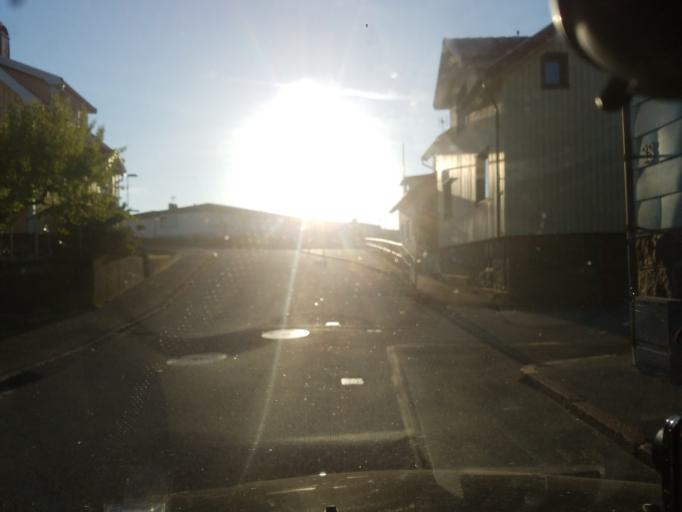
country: SE
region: Vaestra Goetaland
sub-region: Lysekils Kommun
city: Lysekil
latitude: 58.2697
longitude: 11.4275
